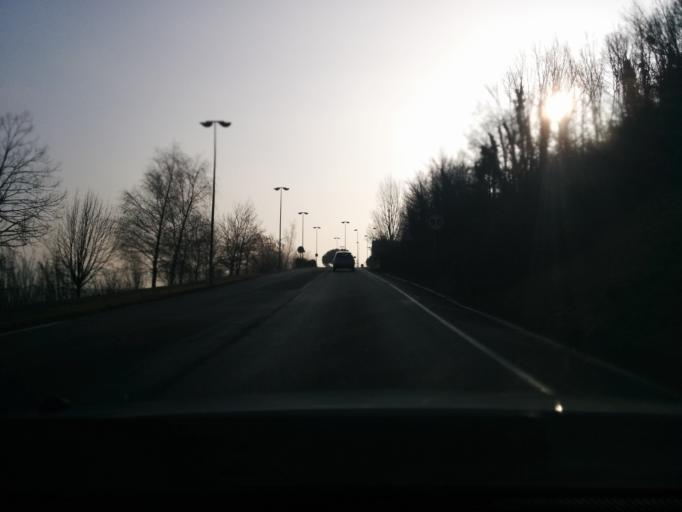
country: ES
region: Navarre
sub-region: Provincia de Navarra
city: Burlata
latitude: 42.8120
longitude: -1.6212
